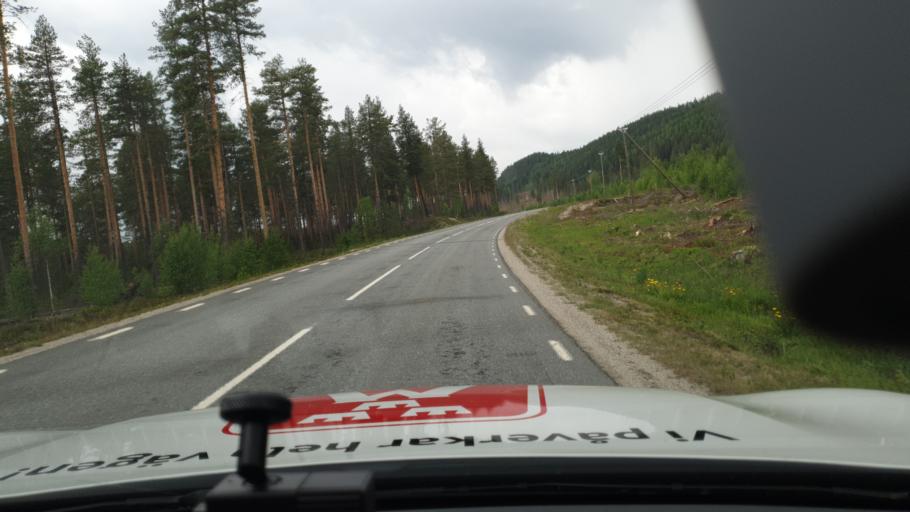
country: SE
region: Vaesterbotten
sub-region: Lycksele Kommun
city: Lycksele
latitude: 64.4082
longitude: 19.0237
